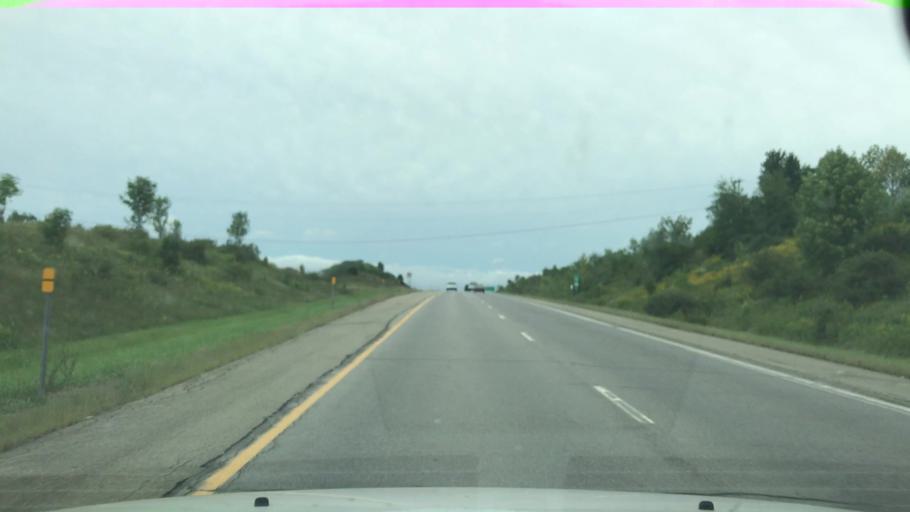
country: US
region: New York
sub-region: Erie County
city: Springville
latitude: 42.5616
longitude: -78.7123
